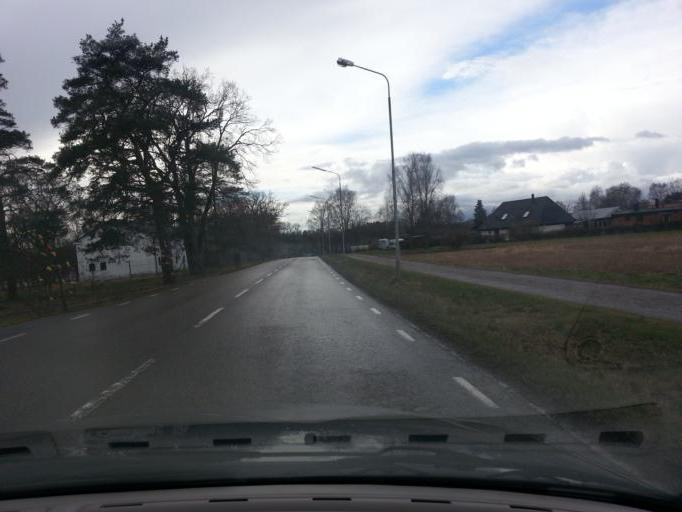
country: SE
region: Skane
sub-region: Klippans Kommun
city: Ljungbyhed
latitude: 56.0813
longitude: 13.2424
